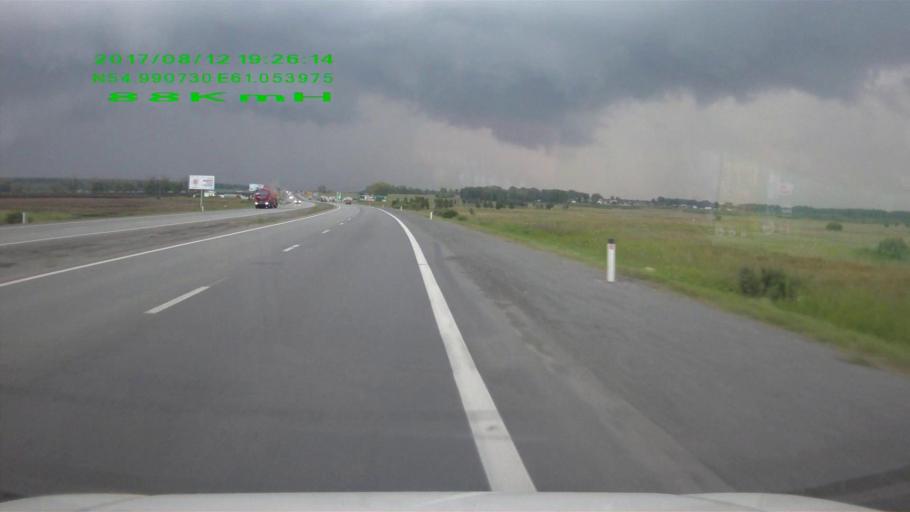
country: RU
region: Chelyabinsk
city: Poletayevo
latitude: 54.9902
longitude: 61.0503
